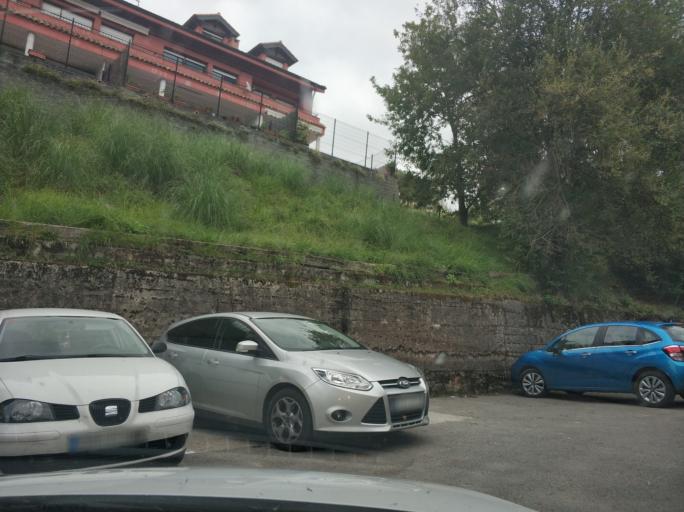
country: ES
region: Cantabria
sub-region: Provincia de Cantabria
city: Comillas
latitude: 43.3827
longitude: -4.2895
